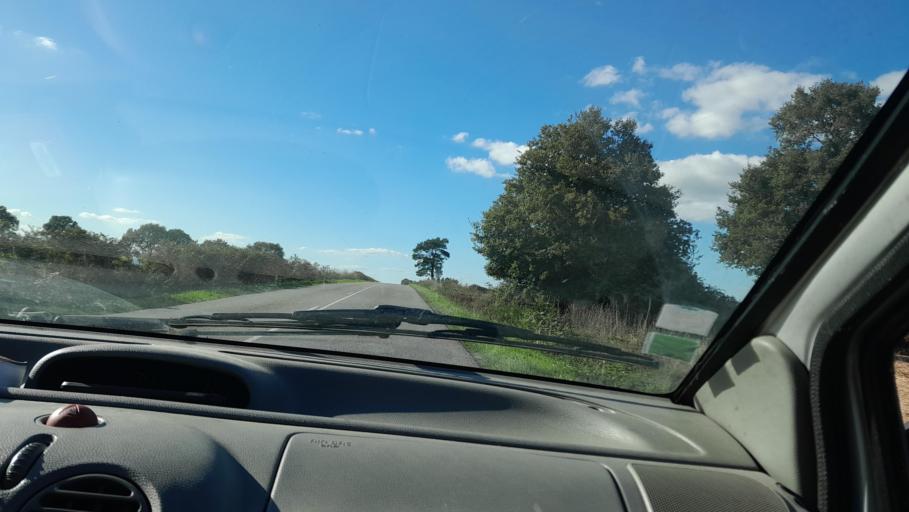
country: FR
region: Pays de la Loire
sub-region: Departement de la Mayenne
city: Quelaines-Saint-Gault
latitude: 47.9332
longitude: -0.8432
